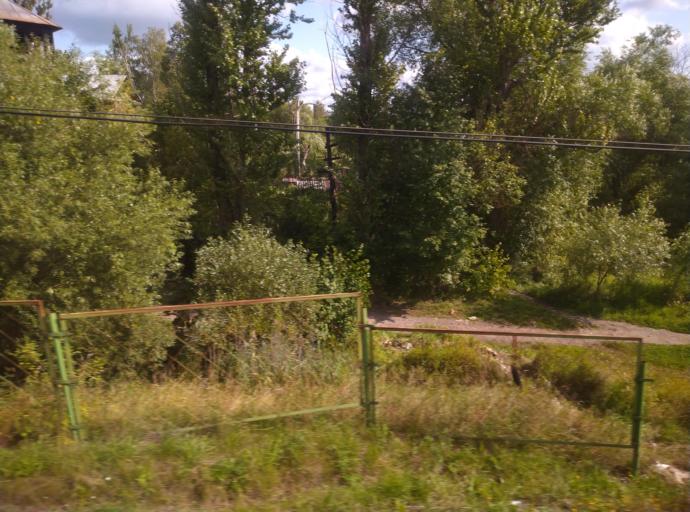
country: RU
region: Leningrad
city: Ul'yanovka
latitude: 59.6366
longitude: 30.7561
